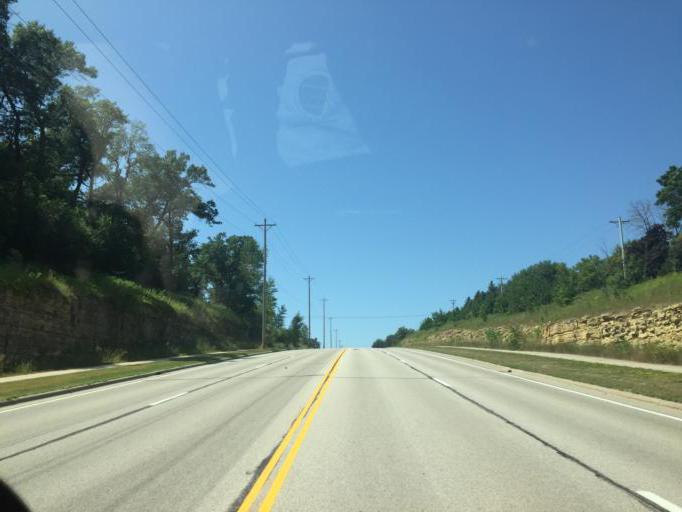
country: US
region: Minnesota
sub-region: Olmsted County
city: Rochester
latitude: 43.9639
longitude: -92.4826
